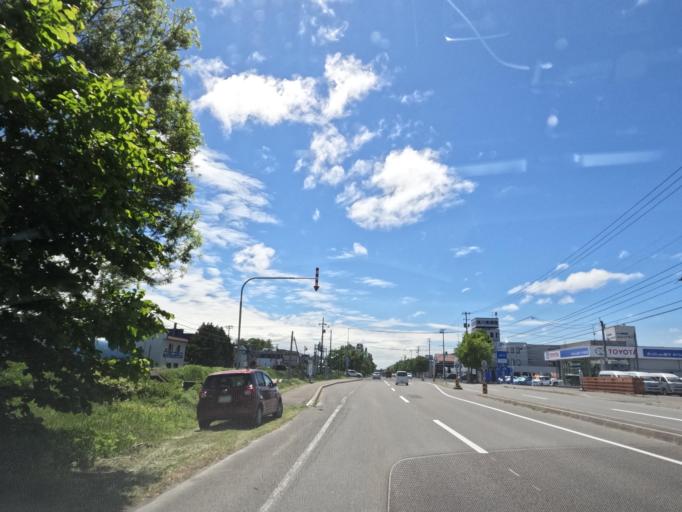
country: JP
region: Hokkaido
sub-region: Asahikawa-shi
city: Asahikawa
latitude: 43.7361
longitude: 142.3626
